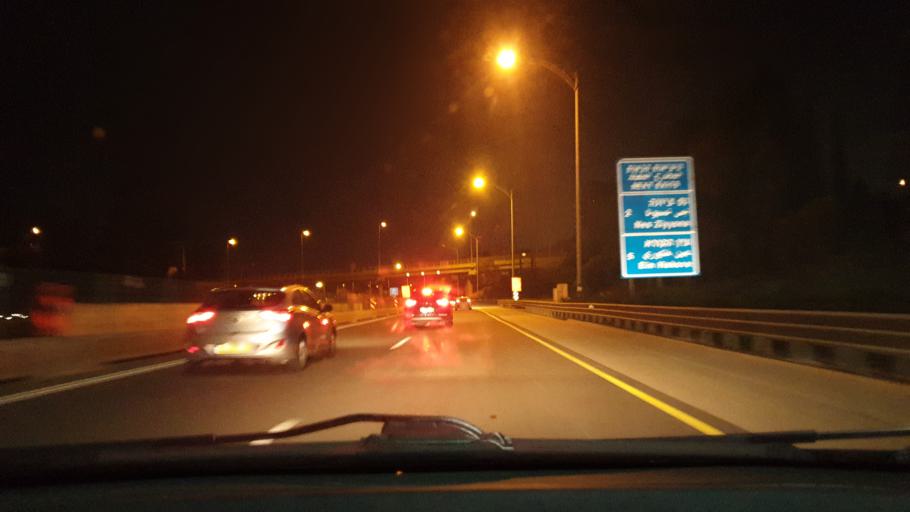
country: IL
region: Central District
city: Ness Ziona
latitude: 31.9265
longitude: 34.8309
